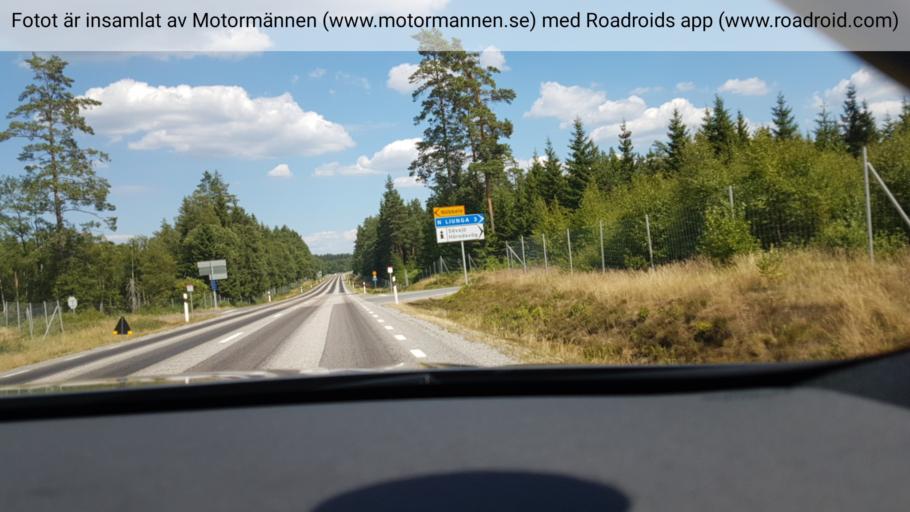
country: SE
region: Joenkoeping
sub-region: Savsjo Kommun
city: Stockaryd
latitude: 57.3778
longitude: 14.5588
